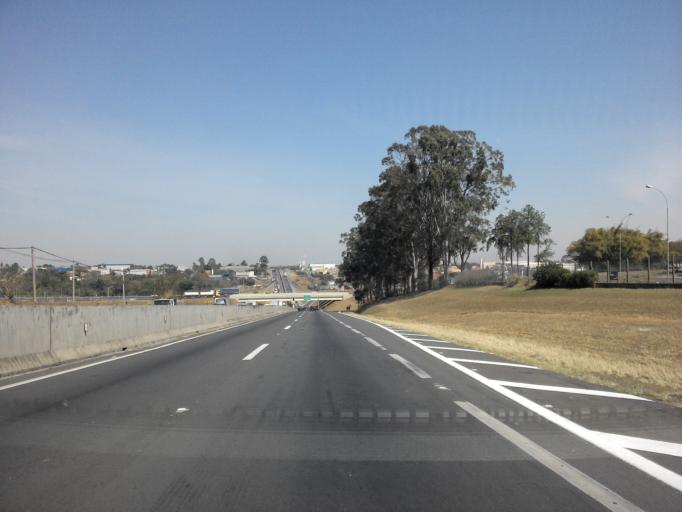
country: BR
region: Sao Paulo
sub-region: Hortolandia
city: Hortolandia
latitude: -22.9018
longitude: -47.2011
